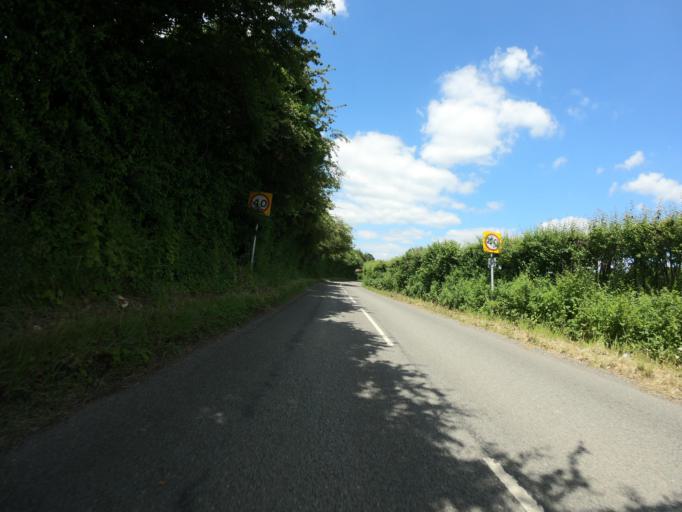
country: GB
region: England
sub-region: Kent
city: Halstead
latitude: 51.3374
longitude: 0.1354
